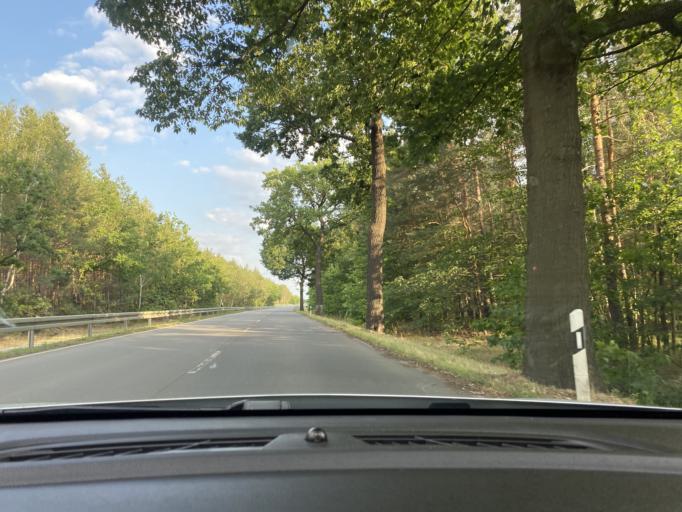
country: DE
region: Saxony
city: Wittichenau
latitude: 51.4122
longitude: 14.2873
